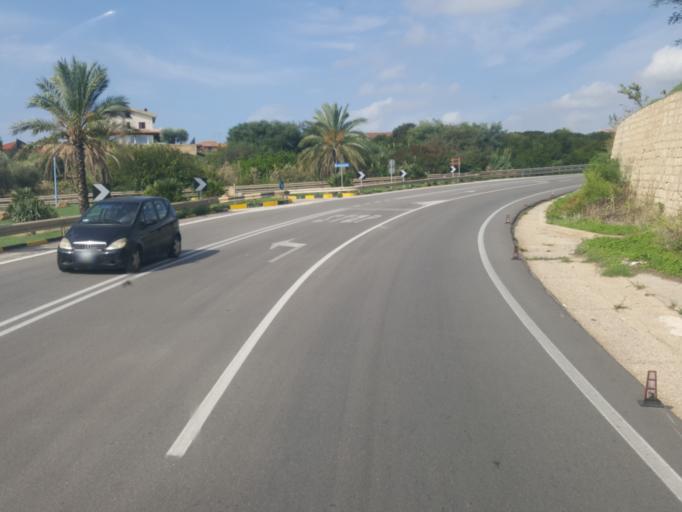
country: IT
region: Sicily
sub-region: Agrigento
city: Porto Empedocle
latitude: 37.2943
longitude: 13.4981
